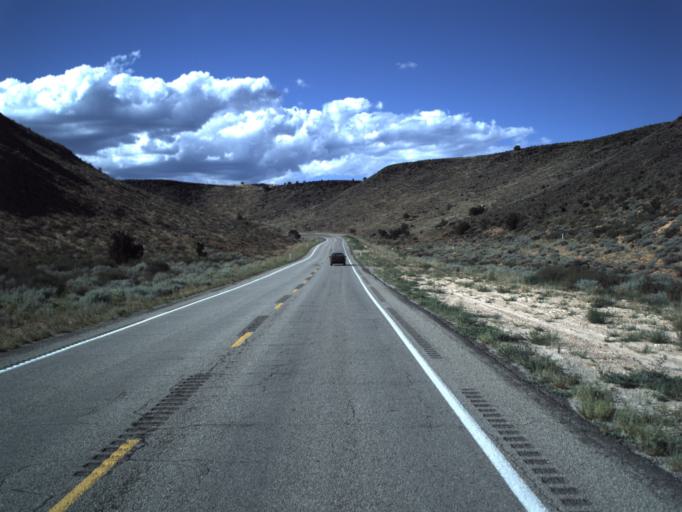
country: US
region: Utah
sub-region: Washington County
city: Toquerville
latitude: 37.2683
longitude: -113.2960
